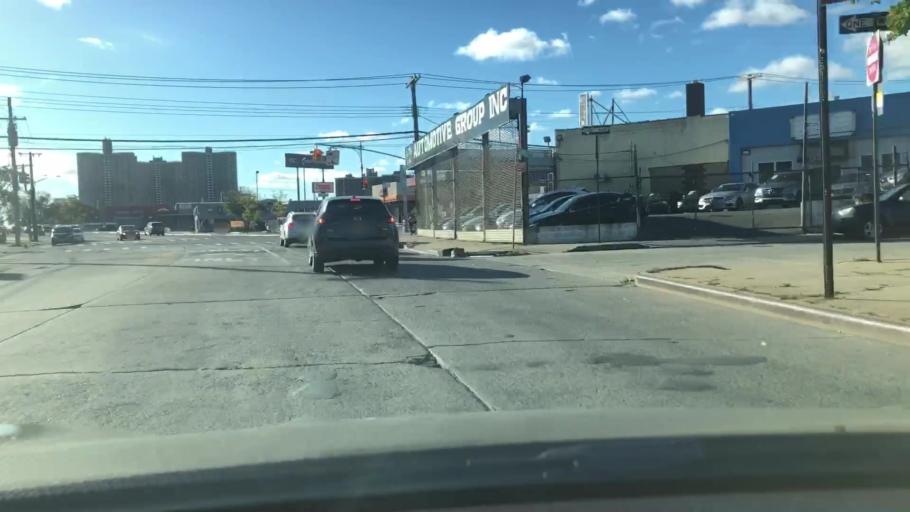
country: US
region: New York
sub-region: Bronx
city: Eastchester
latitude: 40.8865
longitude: -73.8282
